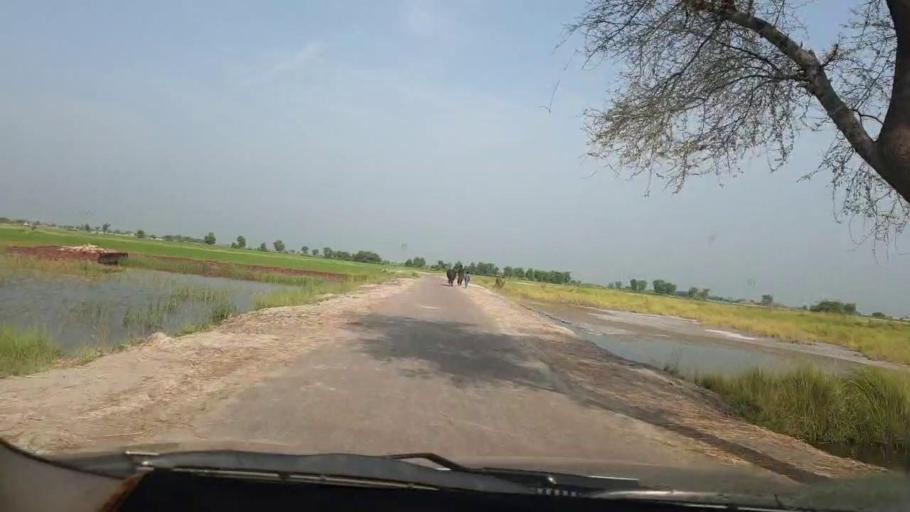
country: PK
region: Sindh
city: Goth Garelo
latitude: 27.4683
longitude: 68.0799
